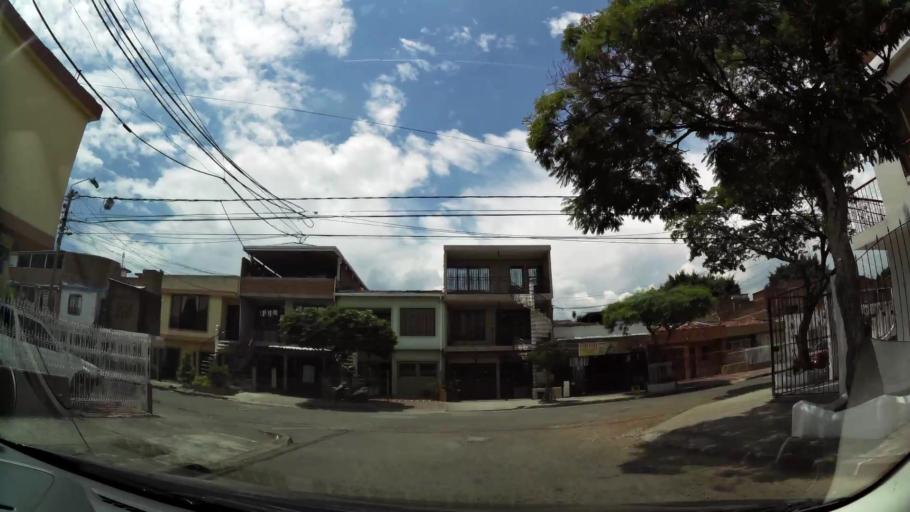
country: CO
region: Valle del Cauca
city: Cali
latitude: 3.4423
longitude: -76.5075
